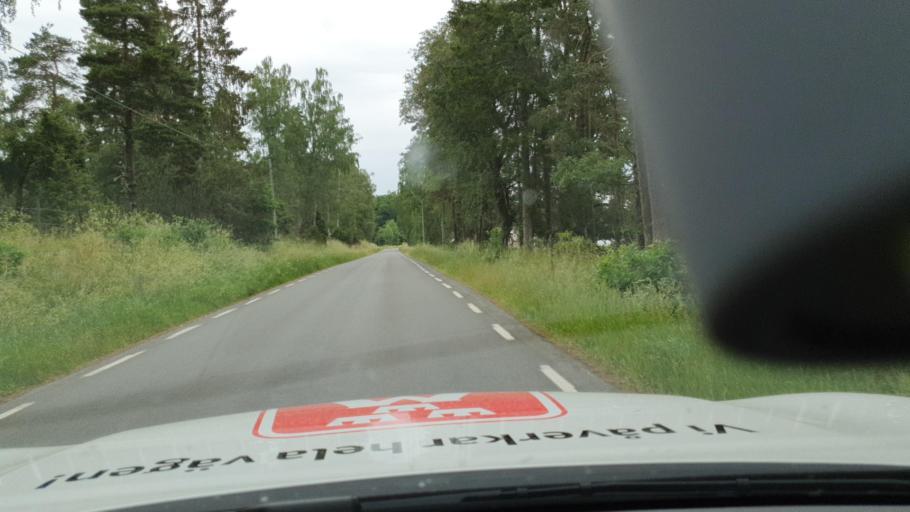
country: SE
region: Vaestra Goetaland
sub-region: Tidaholms Kommun
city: Olofstorp
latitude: 58.3191
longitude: 14.0971
